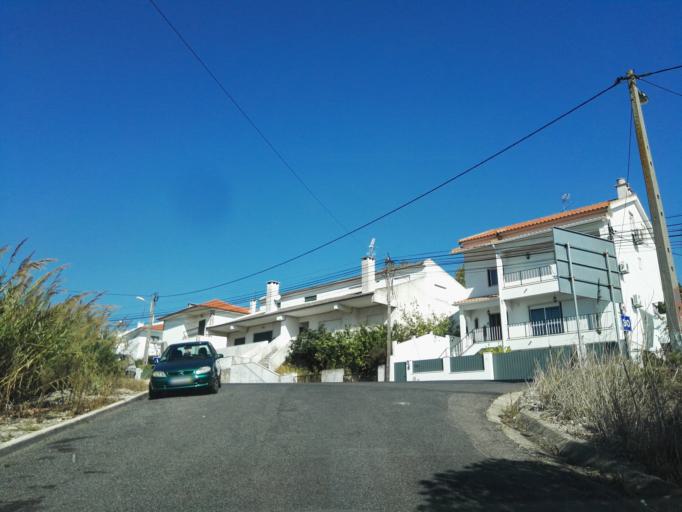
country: PT
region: Lisbon
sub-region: Odivelas
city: Povoa de Santo Adriao
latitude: 38.8038
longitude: -9.1665
